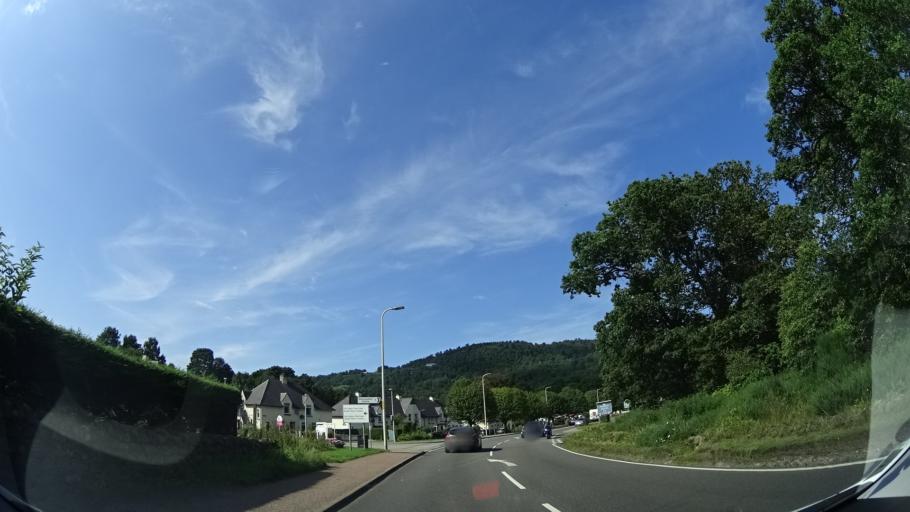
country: GB
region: Scotland
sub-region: Highland
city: Beauly
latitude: 57.3318
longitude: -4.4812
